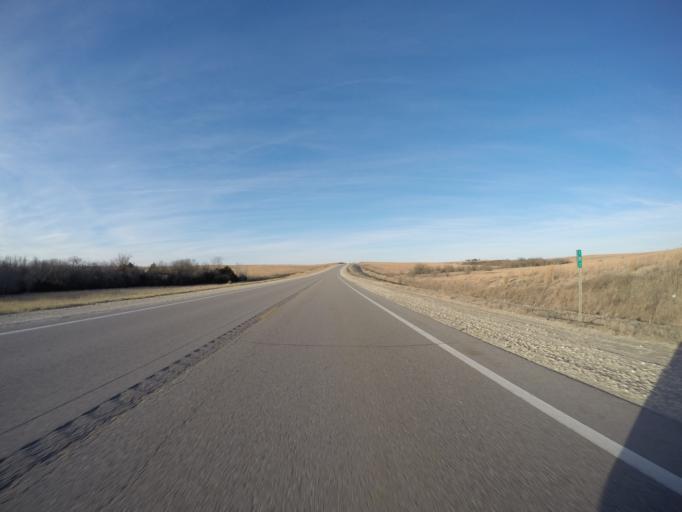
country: US
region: Kansas
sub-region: Marion County
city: Marion
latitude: 38.2939
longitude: -96.9661
